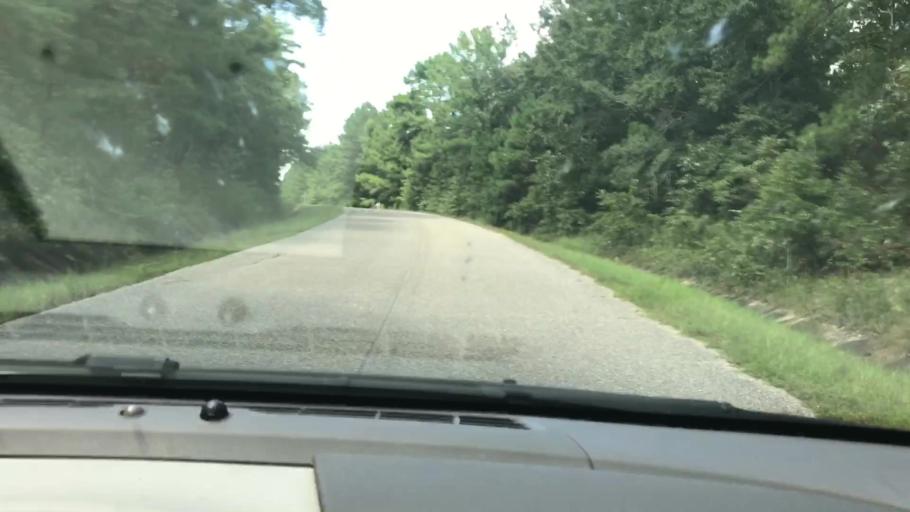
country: US
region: Georgia
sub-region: Clay County
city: Fort Gaines
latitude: 31.7409
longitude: -85.0754
